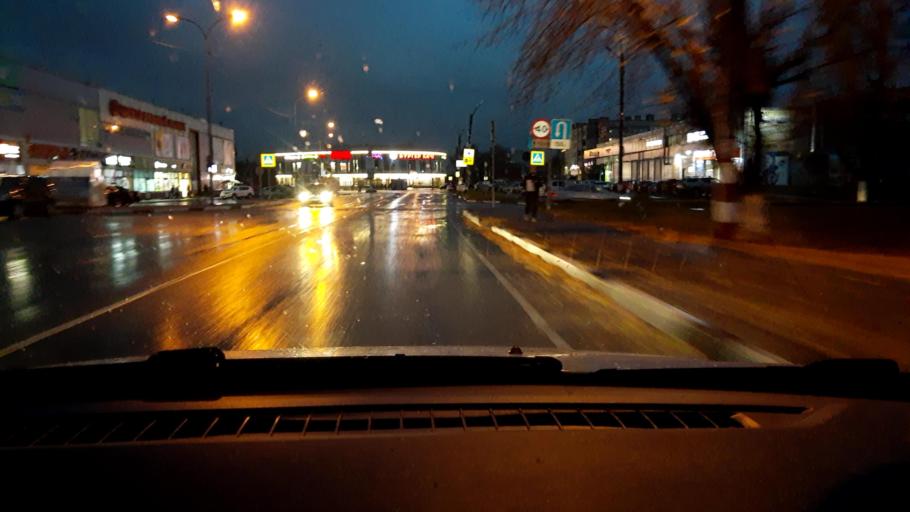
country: RU
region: Nizjnij Novgorod
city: Bor
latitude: 56.3609
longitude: 44.0514
